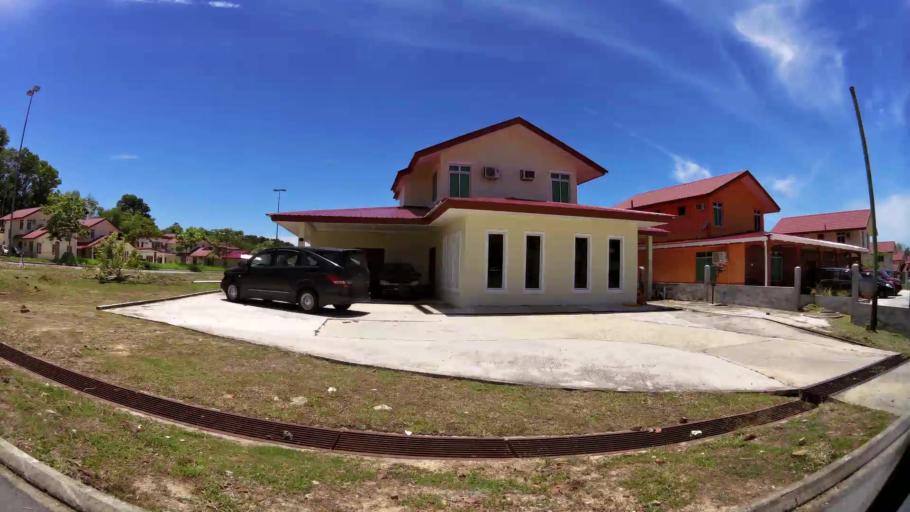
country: BN
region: Brunei and Muara
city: Bandar Seri Begawan
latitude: 5.0221
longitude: 115.0303
